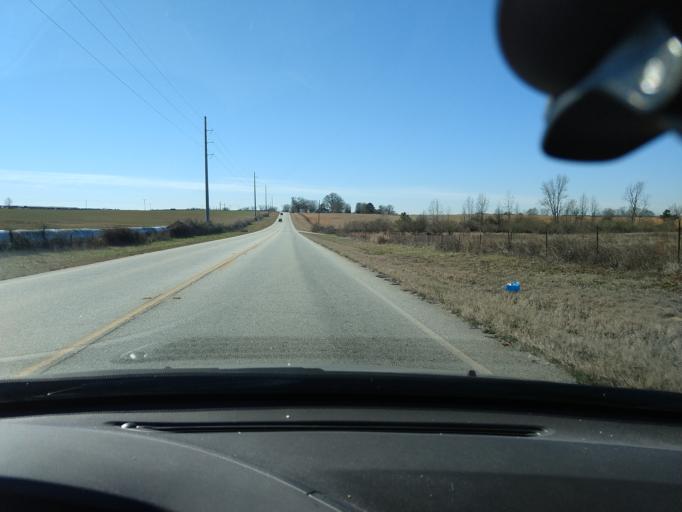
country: US
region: Georgia
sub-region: Newton County
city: Covington
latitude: 33.4959
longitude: -83.7372
